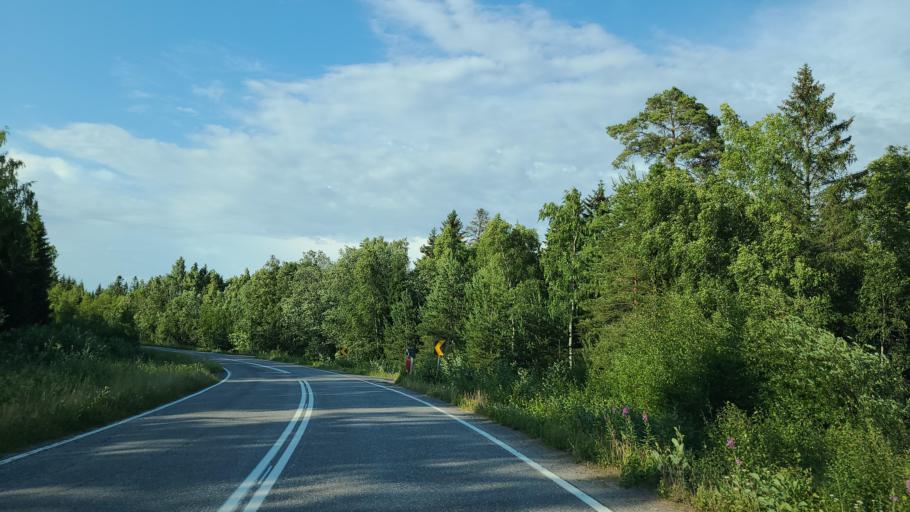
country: FI
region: Ostrobothnia
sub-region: Vaasa
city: Replot
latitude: 63.3074
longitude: 21.3606
